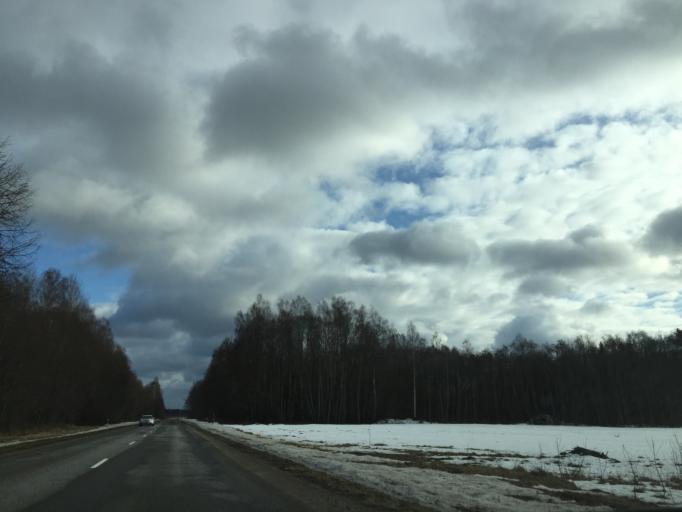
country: LV
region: Aloja
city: Staicele
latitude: 57.8771
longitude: 24.6701
